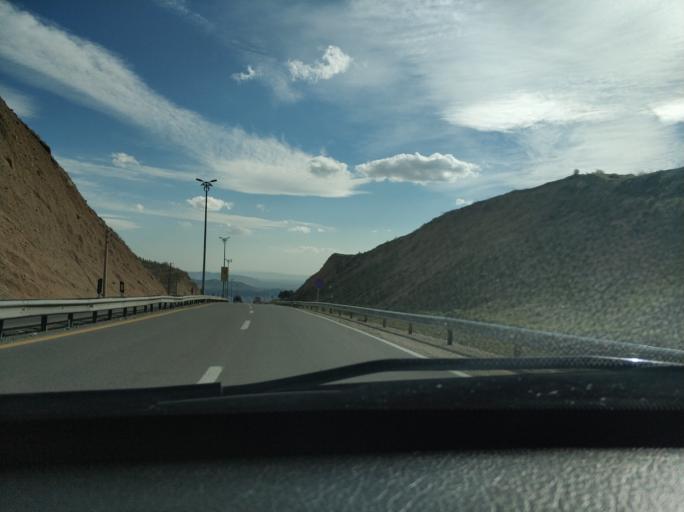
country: IR
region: Tehran
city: Tajrish
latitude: 35.7900
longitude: 51.5678
